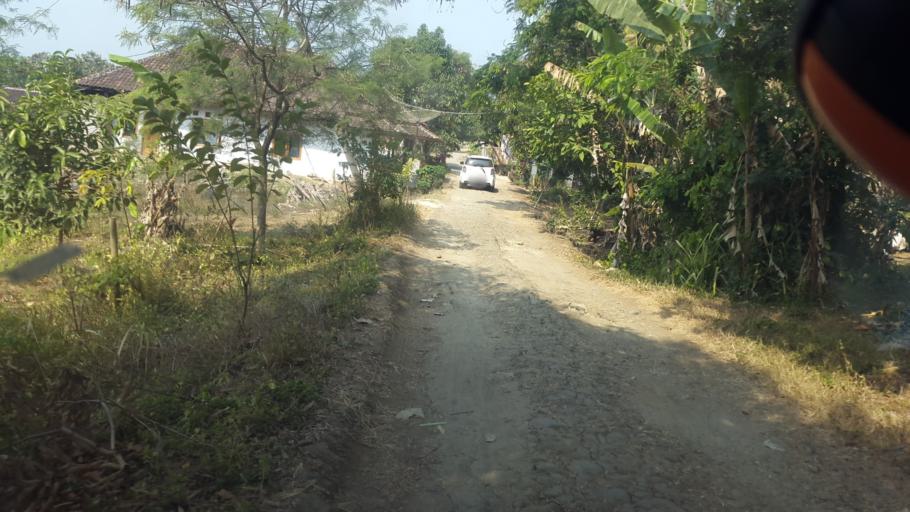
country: ID
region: West Java
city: Babakan Baru
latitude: -7.3265
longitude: 106.6157
